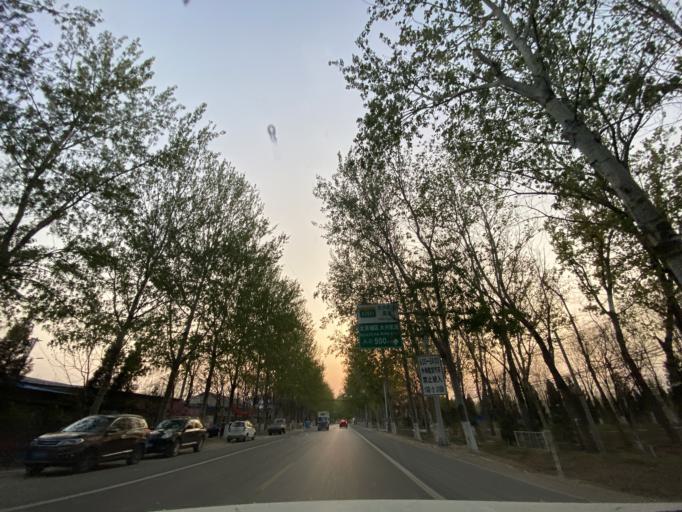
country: CN
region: Beijing
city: Weishanzhuang
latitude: 39.6144
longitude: 116.3850
